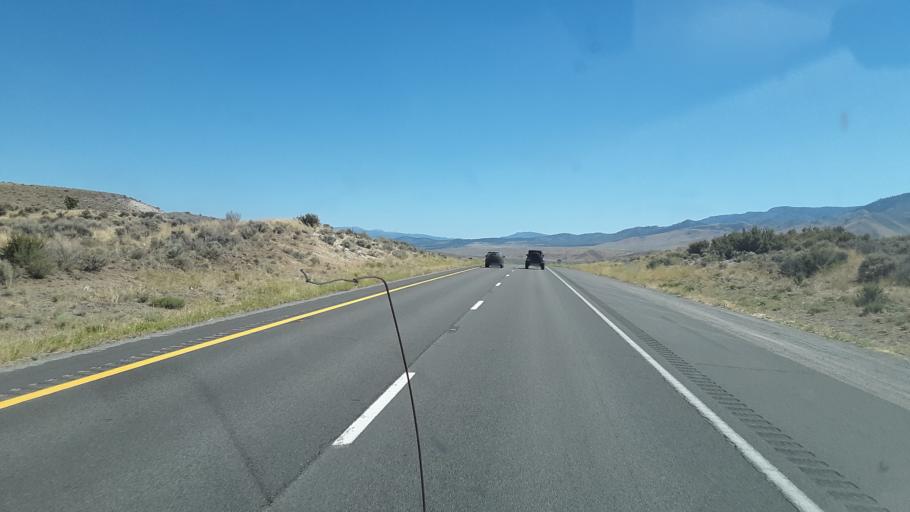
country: US
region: Nevada
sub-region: Washoe County
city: Cold Springs
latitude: 39.7473
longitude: -120.0398
